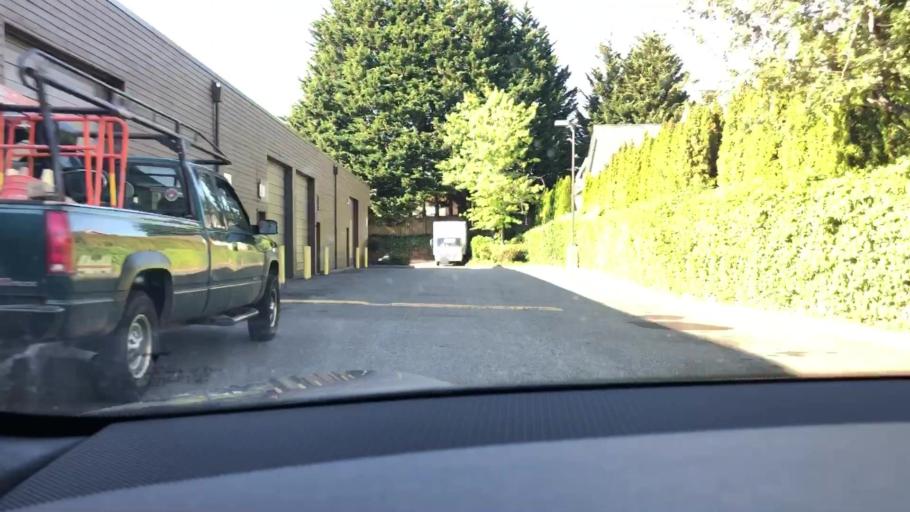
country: US
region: Washington
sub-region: Snohomish County
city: Mill Creek
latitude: 47.9116
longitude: -122.2190
